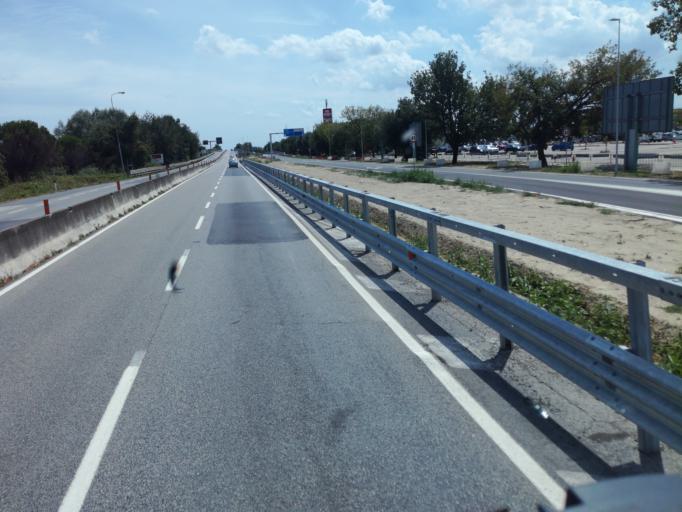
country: IT
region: Emilia-Romagna
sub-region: Provincia di Ravenna
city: Ravenna
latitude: 44.3982
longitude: 12.1814
